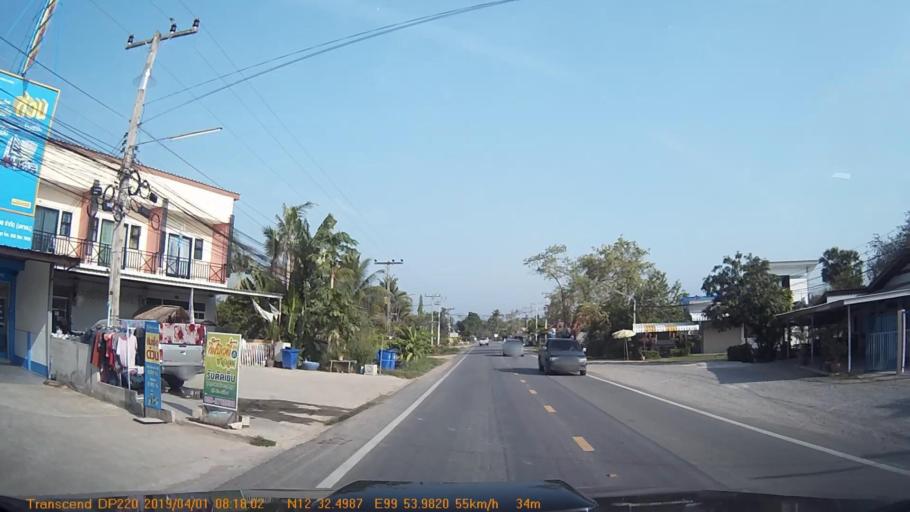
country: TH
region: Prachuap Khiri Khan
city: Hua Hin
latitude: 12.5418
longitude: 99.8996
